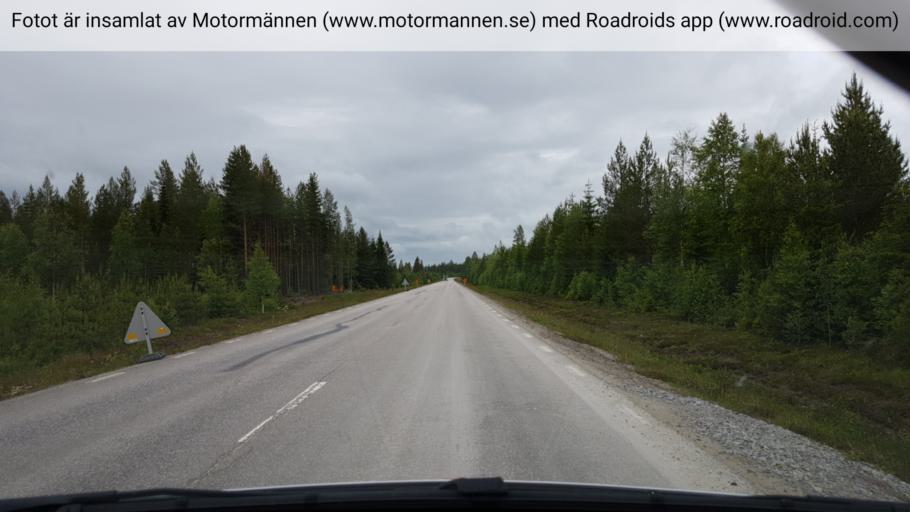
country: SE
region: Vaesterbotten
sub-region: Vindelns Kommun
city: Vindeln
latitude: 64.0673
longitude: 19.6380
